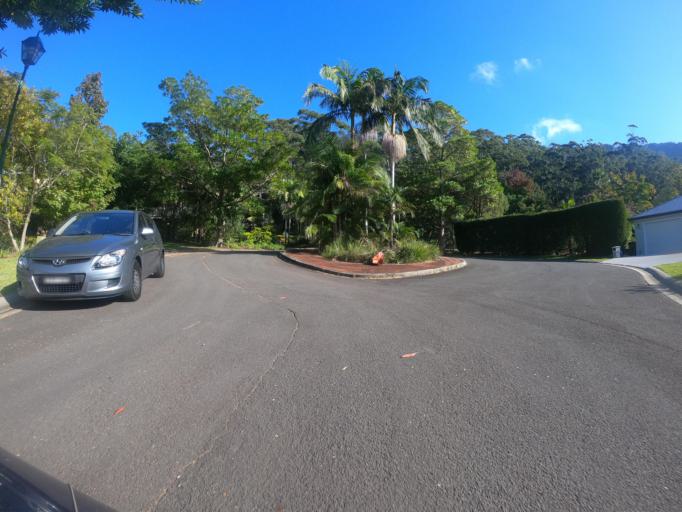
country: AU
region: New South Wales
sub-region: Wollongong
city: Bulli
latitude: -34.3095
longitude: 150.9117
